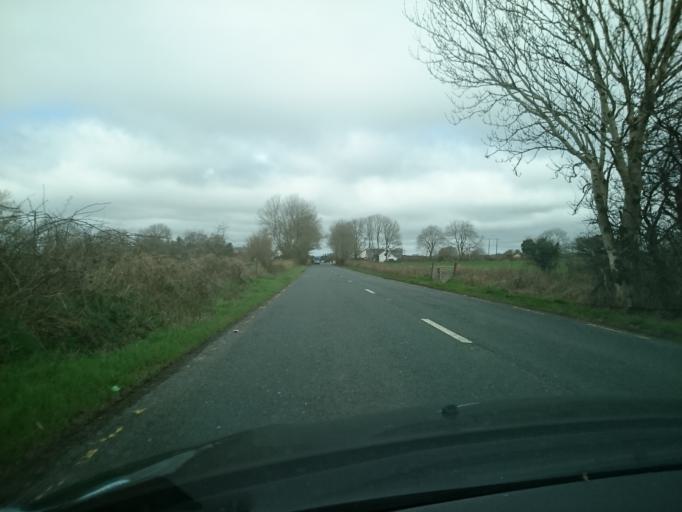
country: IE
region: Connaught
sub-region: Maigh Eo
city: Claremorris
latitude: 53.7486
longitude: -9.0252
